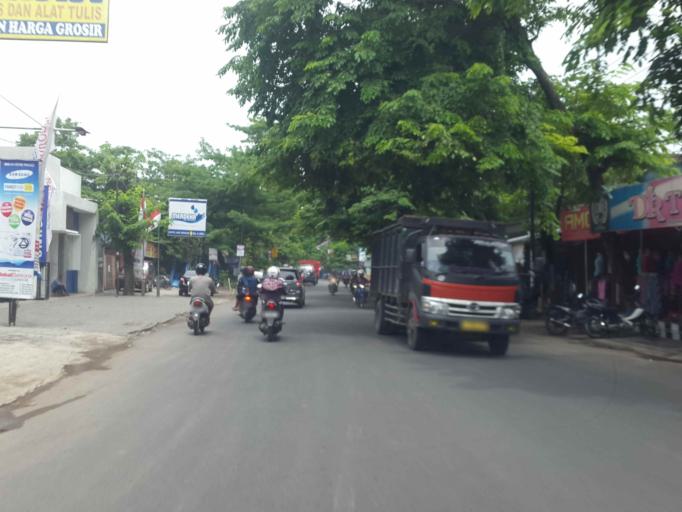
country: ID
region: Central Java
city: Mranggen
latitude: -7.0189
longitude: 110.4710
